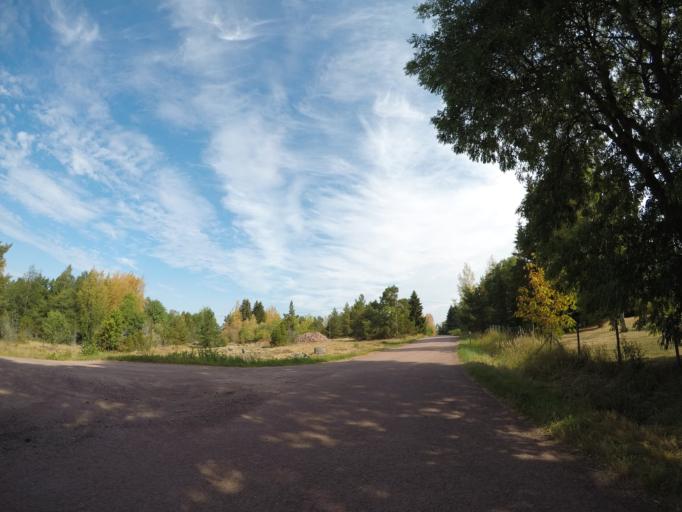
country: AX
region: Alands landsbygd
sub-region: Finstroem
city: Finstroem
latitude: 60.2063
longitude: 19.8738
